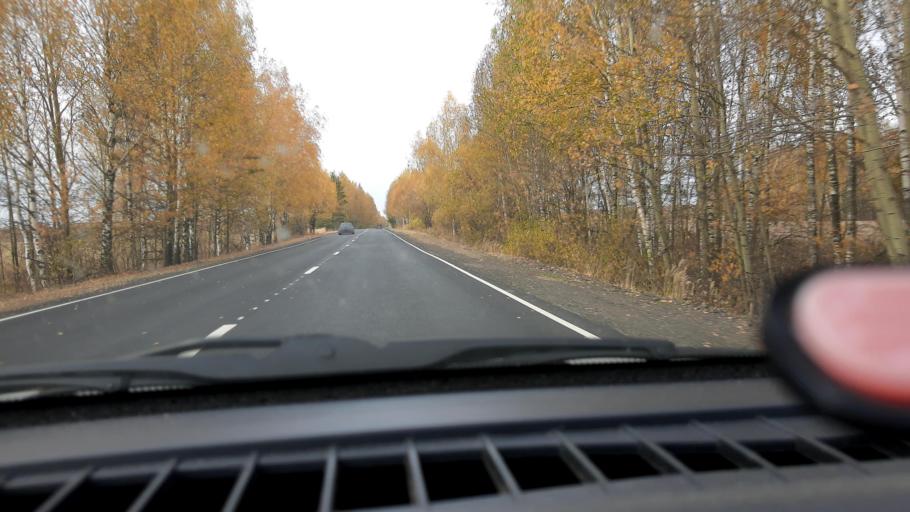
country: RU
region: Nizjnij Novgorod
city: Novaya Balakhna
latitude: 56.5564
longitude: 43.7381
